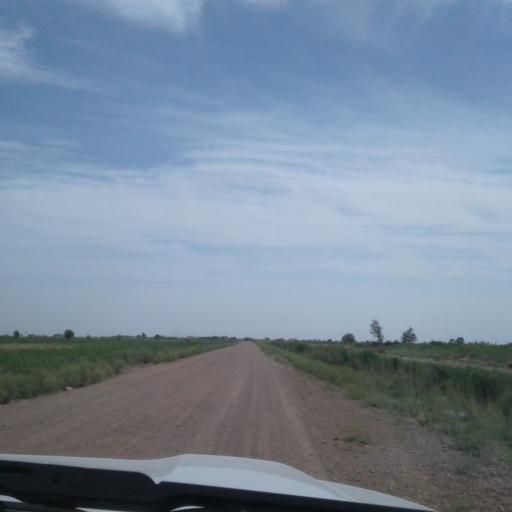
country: TM
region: Dasoguz
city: Tagta
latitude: 41.5423
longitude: 59.8088
